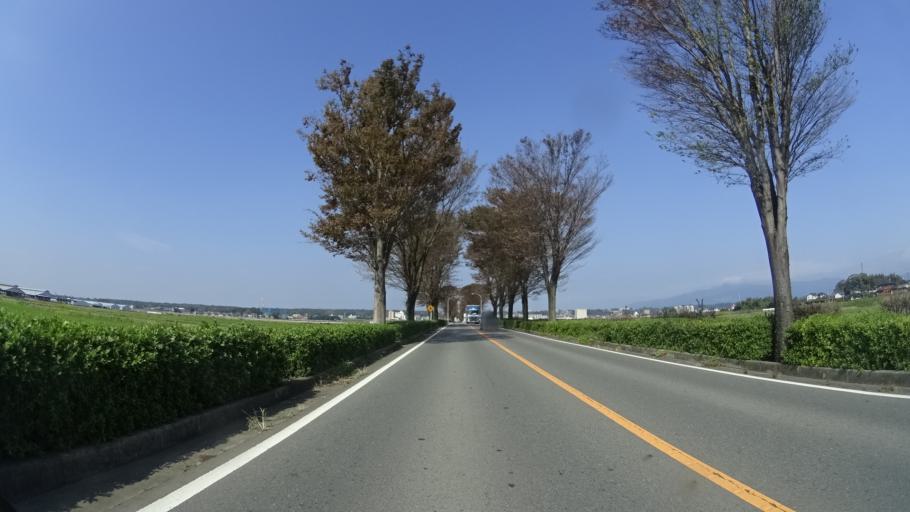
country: JP
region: Kumamoto
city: Ozu
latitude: 32.8627
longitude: 130.8553
